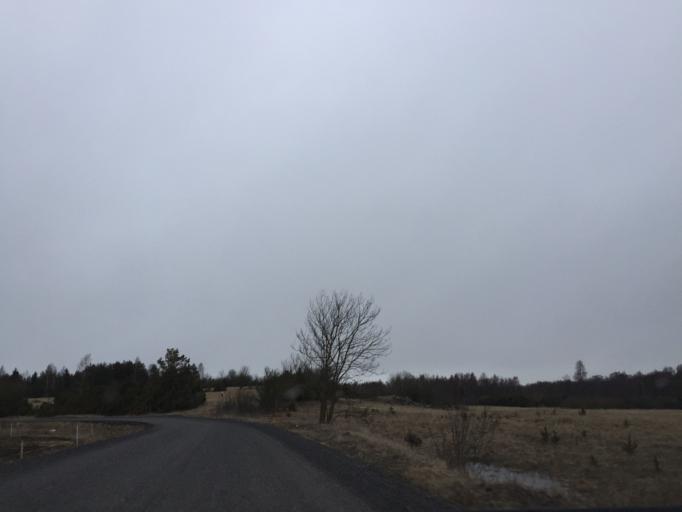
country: EE
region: Laeaene
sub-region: Haapsalu linn
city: Haapsalu
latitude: 58.6760
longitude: 23.5442
